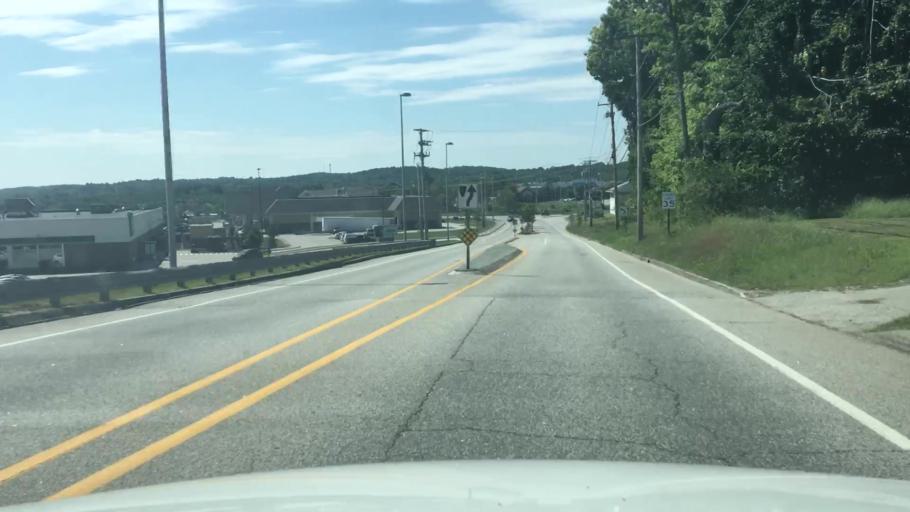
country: US
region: Maine
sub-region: Androscoggin County
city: Auburn
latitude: 44.1239
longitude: -70.2313
